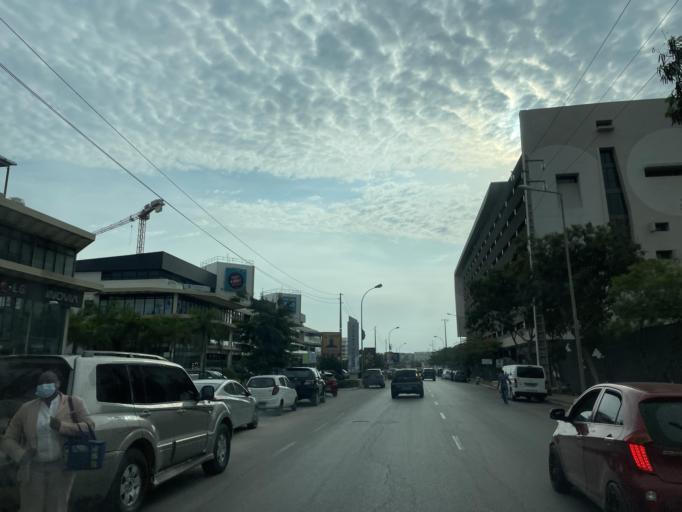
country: AO
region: Luanda
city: Luanda
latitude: -8.9185
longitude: 13.1866
